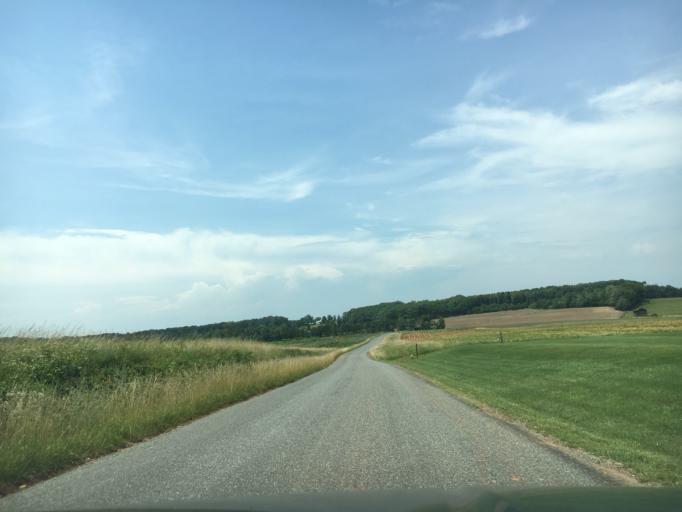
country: US
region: Virginia
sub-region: Pittsylvania County
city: Chatham
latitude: 36.8962
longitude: -79.4074
